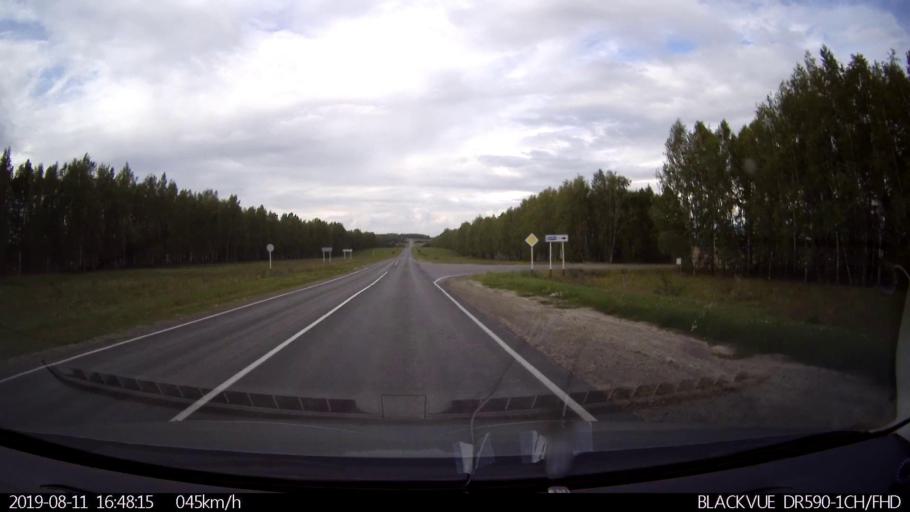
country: RU
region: Ulyanovsk
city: Mayna
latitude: 54.2075
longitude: 47.6918
